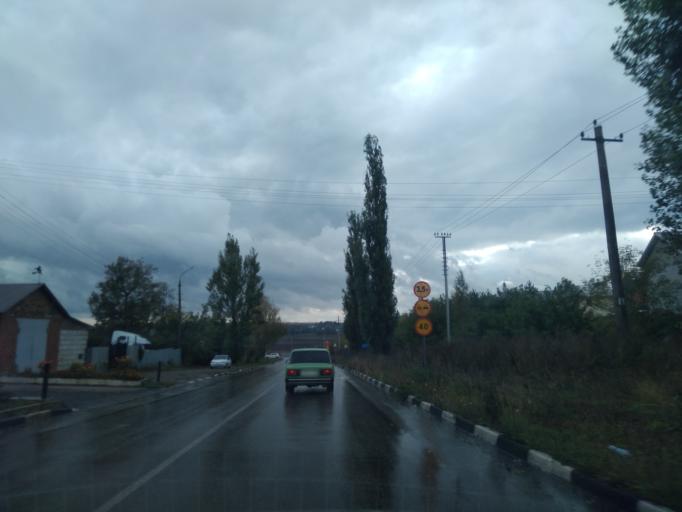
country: RU
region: Tula
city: Yefremov
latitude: 53.1320
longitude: 38.1182
